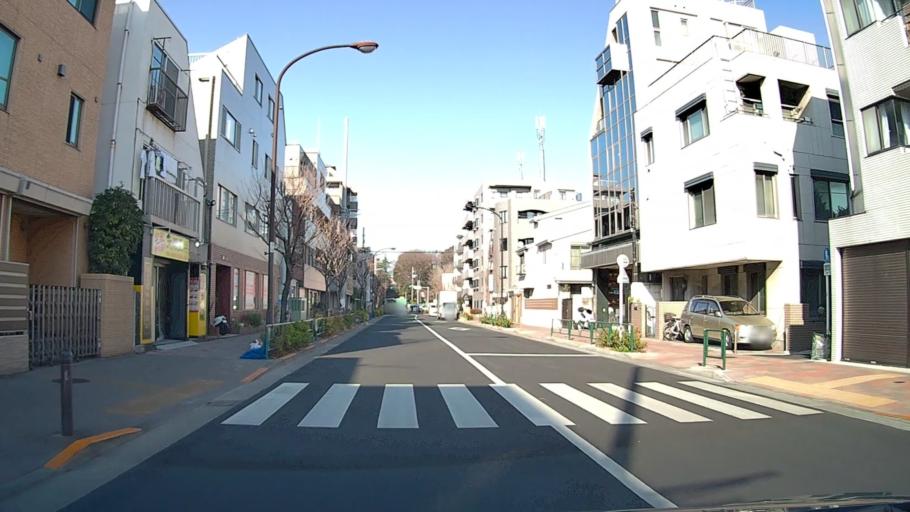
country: JP
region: Tokyo
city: Tokyo
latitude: 35.7153
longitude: 139.6355
